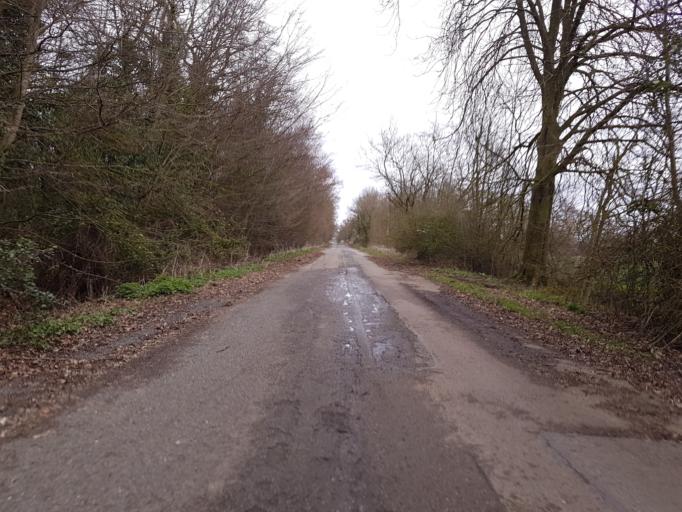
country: GB
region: England
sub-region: Cambridgeshire
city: Girton
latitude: 52.2338
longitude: 0.0523
